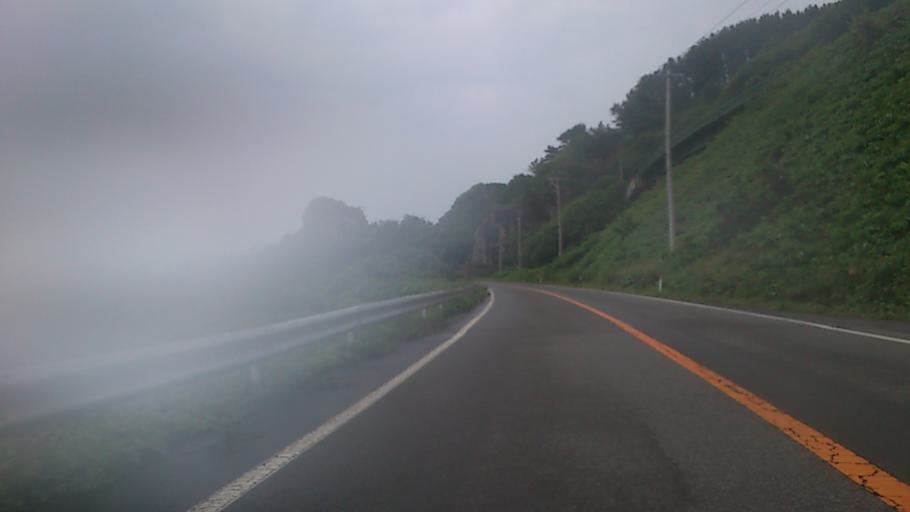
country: JP
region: Akita
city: Noshiromachi
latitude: 40.4434
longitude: 139.9403
